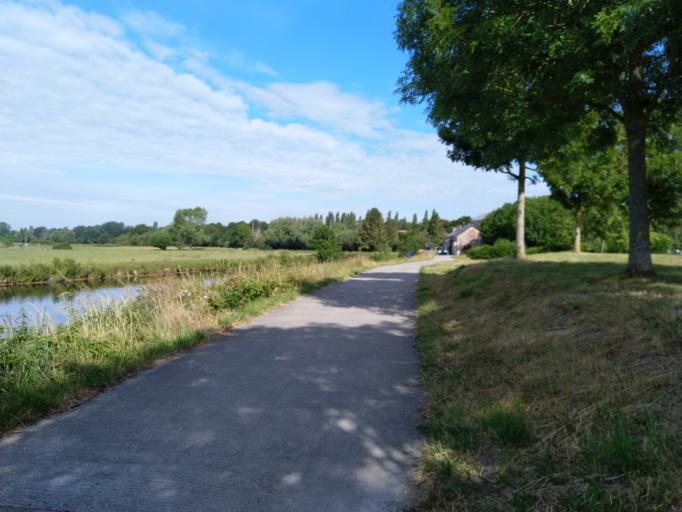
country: FR
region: Nord-Pas-de-Calais
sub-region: Departement du Nord
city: Rousies
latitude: 50.2843
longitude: 4.0142
